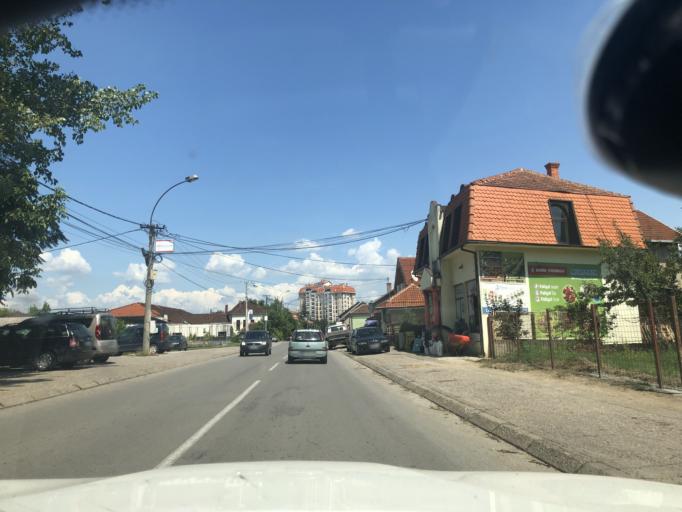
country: RS
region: Central Serbia
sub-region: Jablanicki Okrug
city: Leskovac
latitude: 42.9926
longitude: 21.9314
